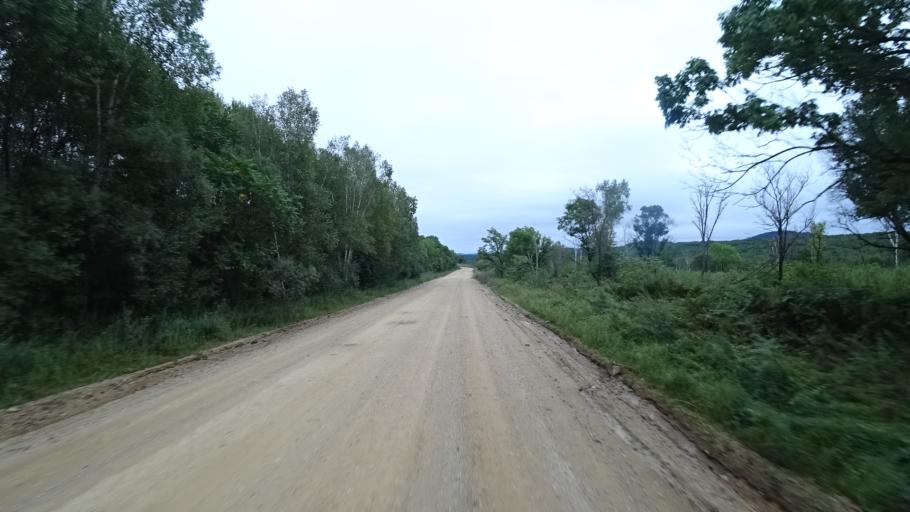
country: RU
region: Primorskiy
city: Rettikhovka
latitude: 44.1785
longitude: 132.8268
